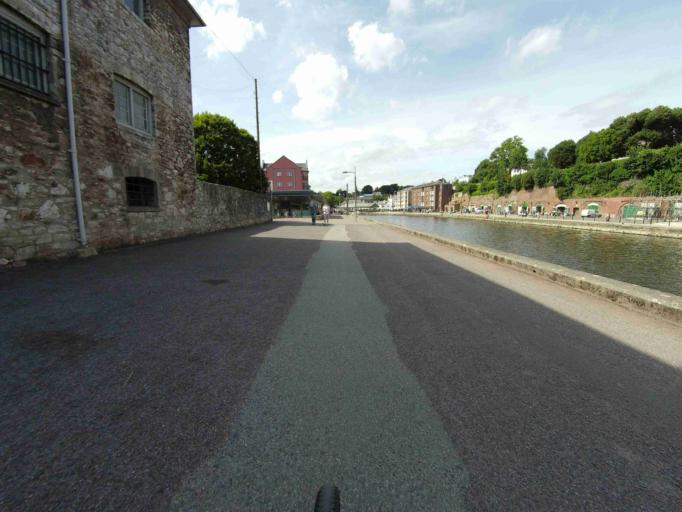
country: GB
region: England
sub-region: Devon
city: Exeter
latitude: 50.7170
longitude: -3.5293
